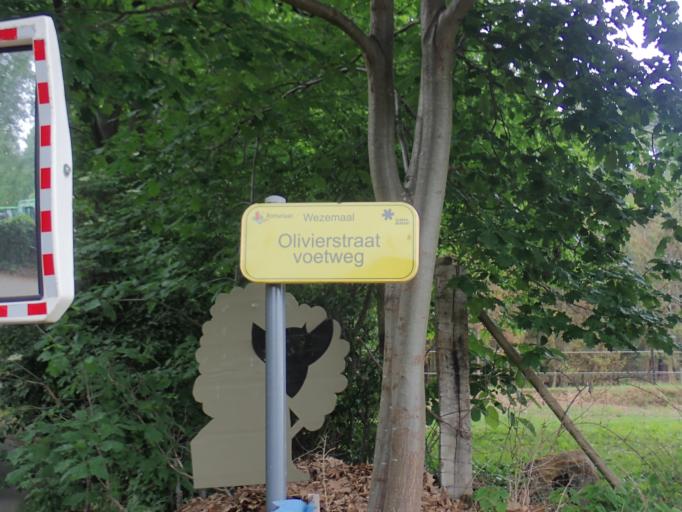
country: BE
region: Flanders
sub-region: Provincie Vlaams-Brabant
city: Holsbeek
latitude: 50.9591
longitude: 4.7687
